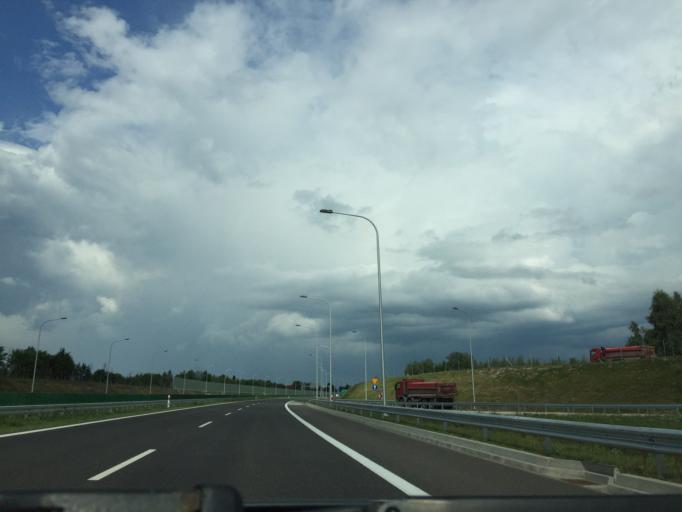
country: PL
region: Masovian Voivodeship
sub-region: Powiat szydlowiecki
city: Szydlowiec
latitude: 51.2380
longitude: 20.8753
